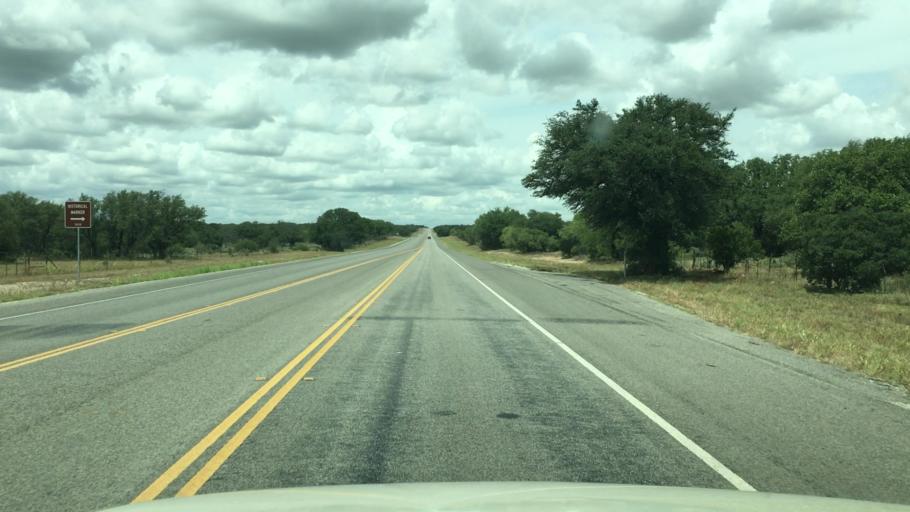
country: US
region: Texas
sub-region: McCulloch County
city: Brady
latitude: 31.0214
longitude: -99.2161
